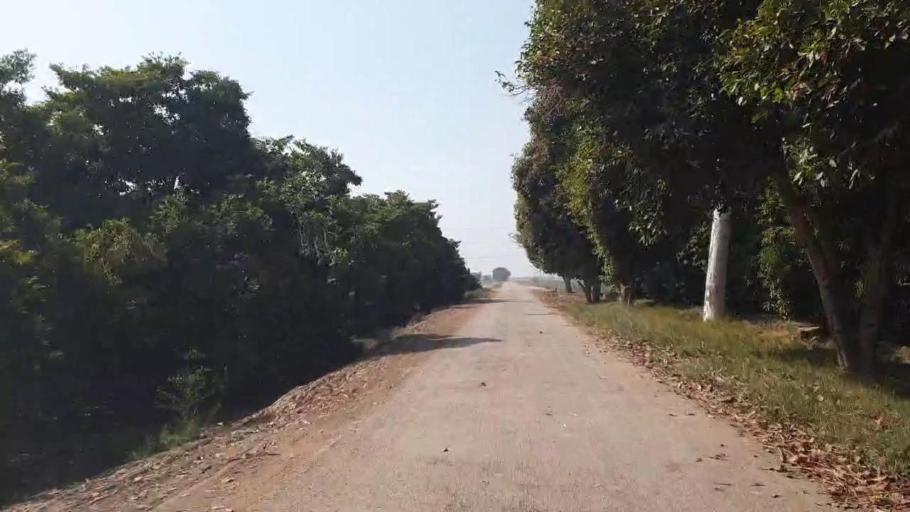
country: PK
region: Sindh
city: Chambar
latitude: 25.3811
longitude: 68.8948
